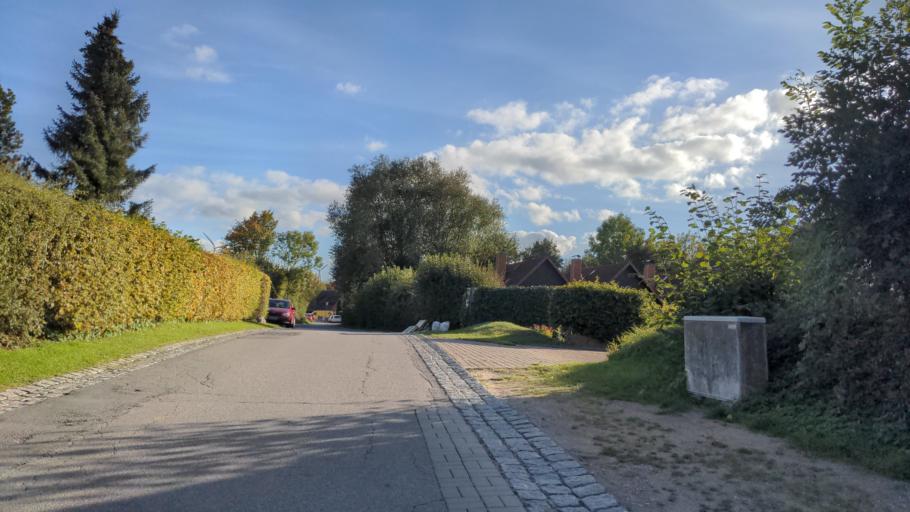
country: DE
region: Schleswig-Holstein
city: Schashagen
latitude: 54.1603
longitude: 10.9127
